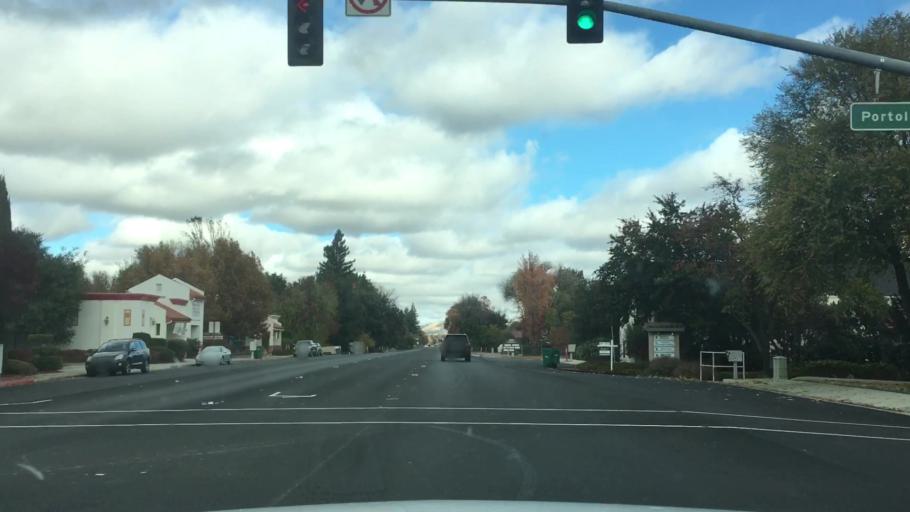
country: US
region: California
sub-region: San Luis Obispo County
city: Atascadero
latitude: 35.4691
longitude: -120.6698
